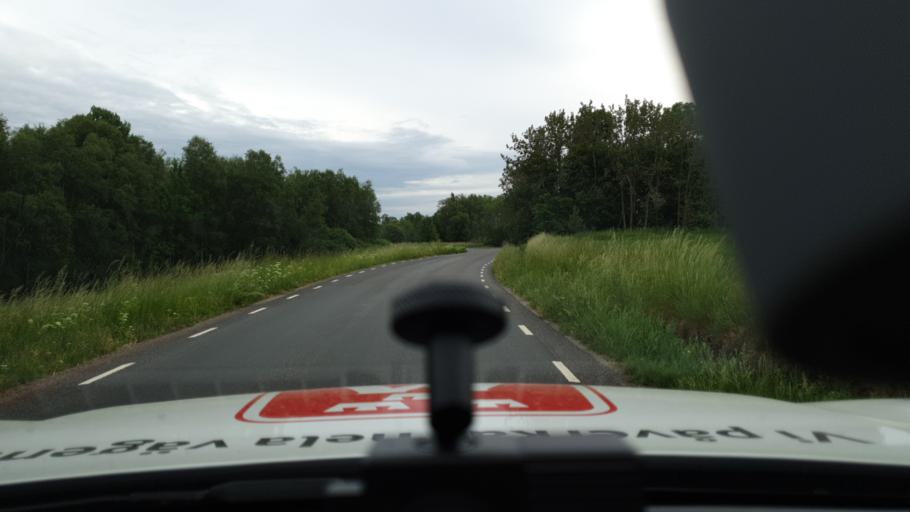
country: SE
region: Vaestra Goetaland
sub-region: Falkopings Kommun
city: Falkoeping
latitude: 58.0794
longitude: 13.6359
